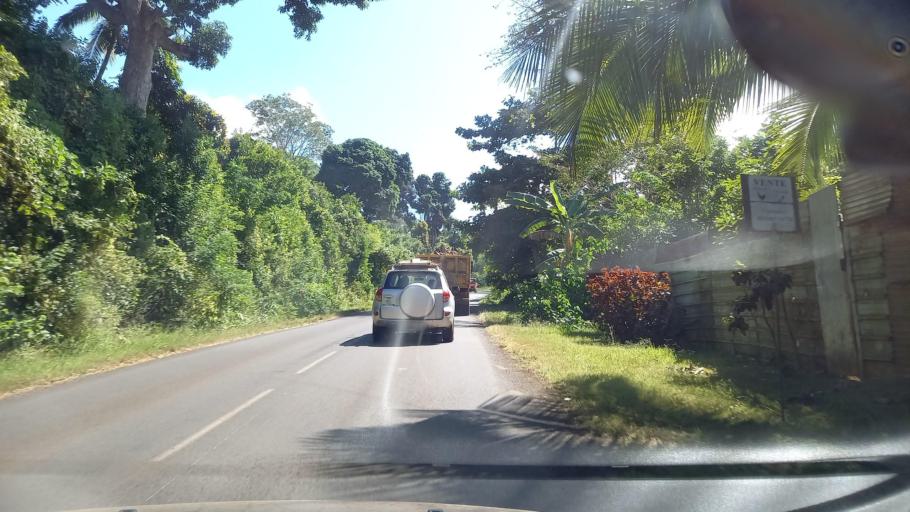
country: YT
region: M'Tsangamouji
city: M'Tsangamouji
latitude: -12.7536
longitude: 45.0932
